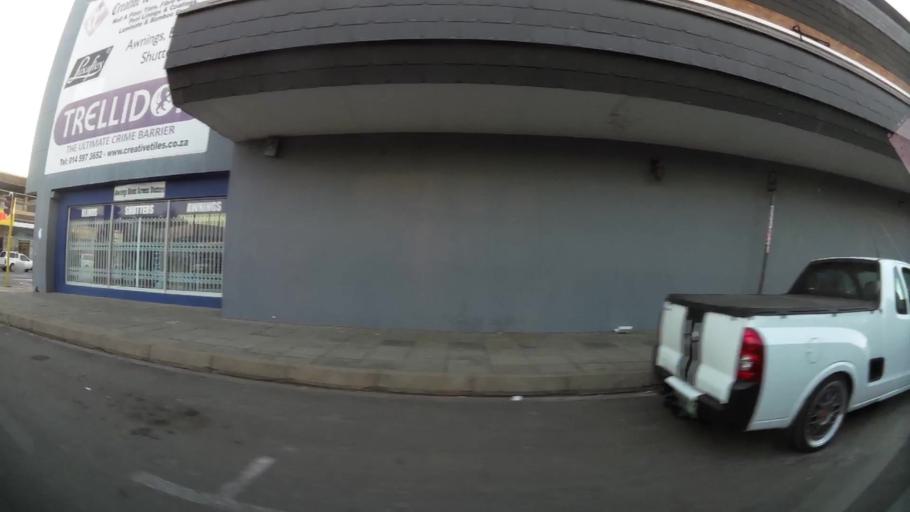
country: ZA
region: North-West
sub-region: Bojanala Platinum District Municipality
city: Rustenburg
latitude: -25.6711
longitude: 27.2418
